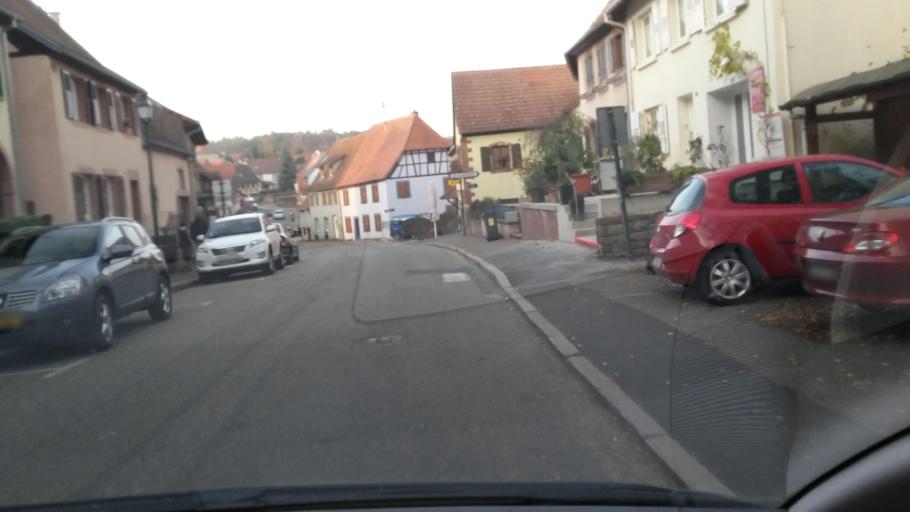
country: FR
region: Alsace
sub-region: Departement du Bas-Rhin
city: Neuwiller-les-Saverne
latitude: 48.8589
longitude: 7.3208
